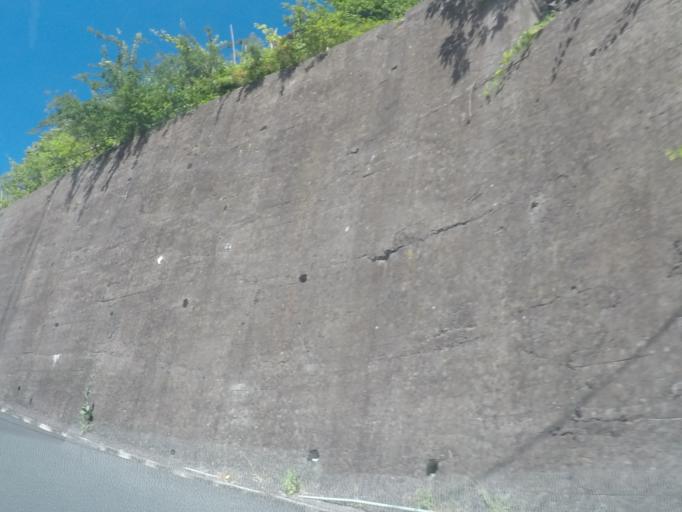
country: PT
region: Madeira
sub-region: Camara de Lobos
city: Curral das Freiras
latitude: 32.7156
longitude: -16.9672
